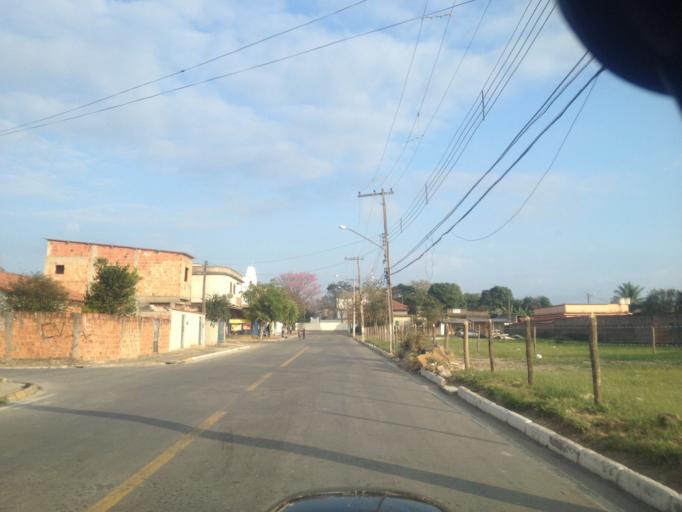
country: BR
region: Rio de Janeiro
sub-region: Porto Real
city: Porto Real
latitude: -22.4434
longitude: -44.3103
